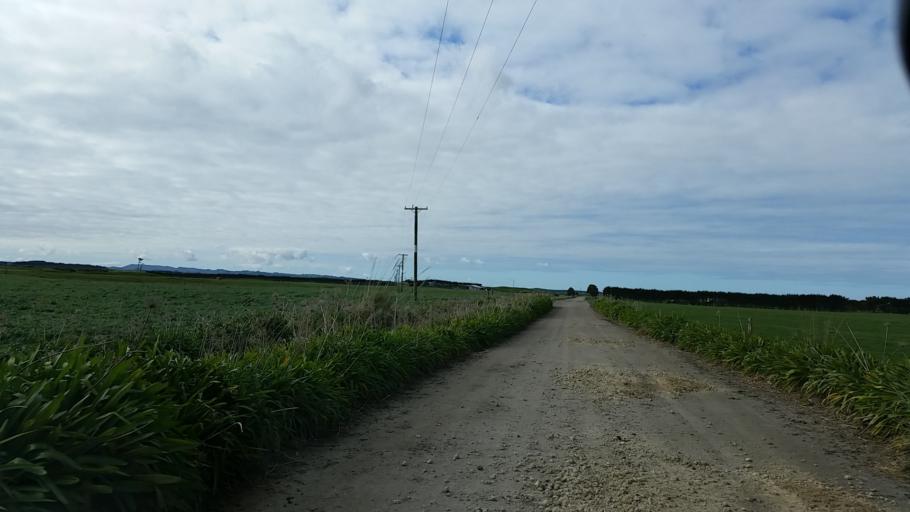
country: NZ
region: Taranaki
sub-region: South Taranaki District
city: Patea
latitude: -39.8247
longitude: 174.6513
